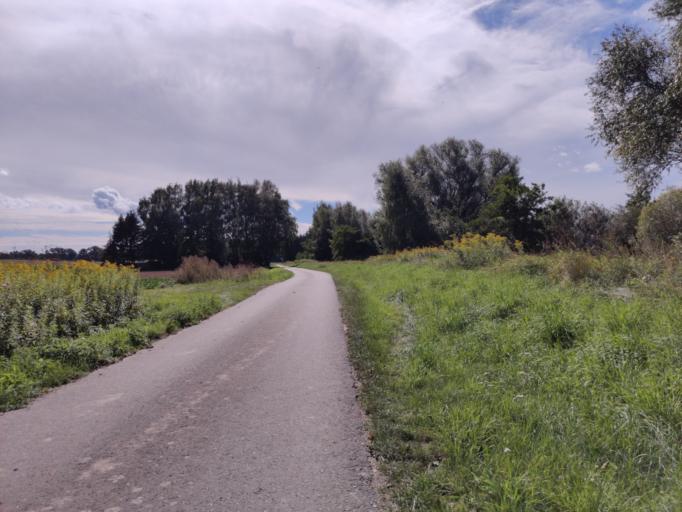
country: DE
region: Lower Saxony
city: Heere
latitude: 52.0650
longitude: 10.2616
